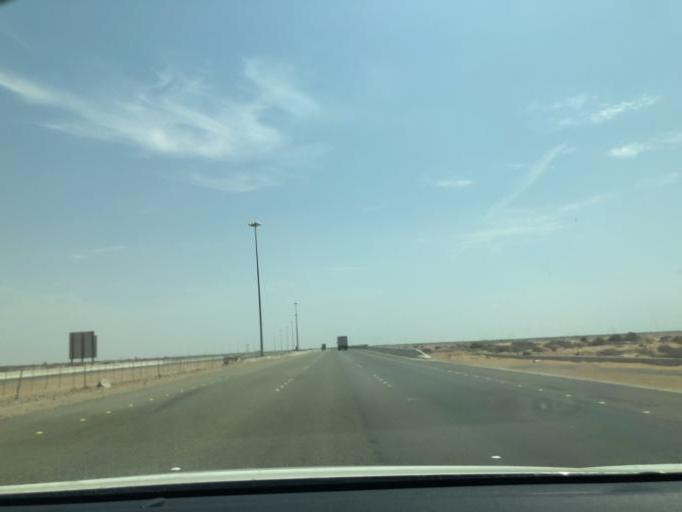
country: SA
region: Makkah
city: Rabigh
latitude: 22.2540
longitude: 39.1169
